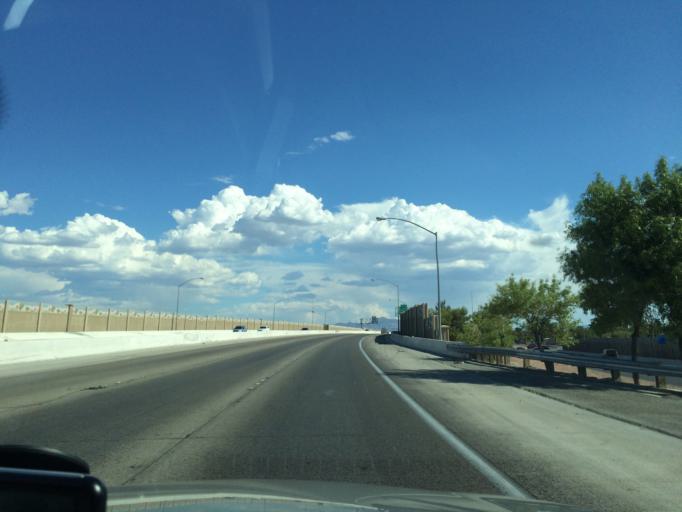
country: US
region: Nevada
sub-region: Clark County
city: Winchester
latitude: 36.1616
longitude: -115.0923
